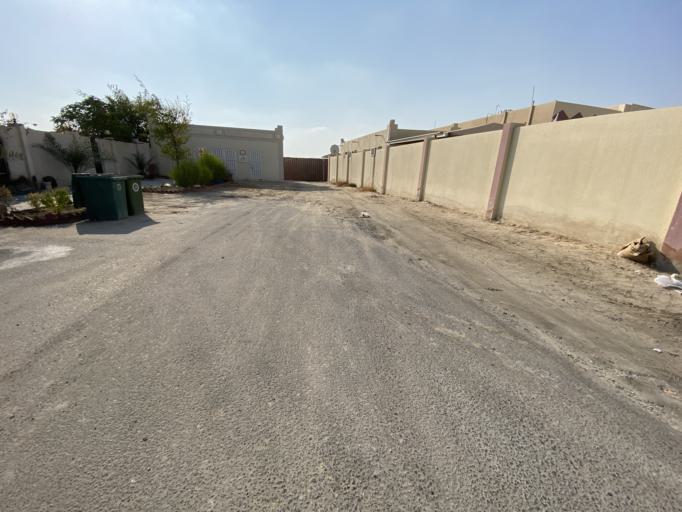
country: QA
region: Baladiyat ar Rayyan
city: Ar Rayyan
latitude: 25.2327
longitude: 51.3758
